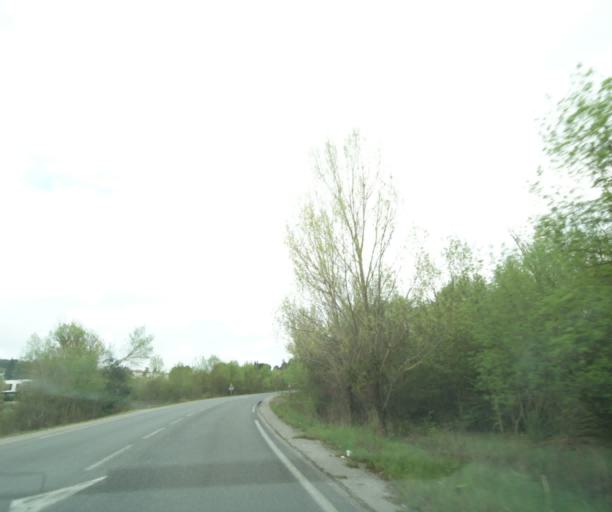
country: FR
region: Languedoc-Roussillon
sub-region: Departement de l'Herault
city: Saint-Jean-de-Vedas
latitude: 43.5846
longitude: 3.8192
